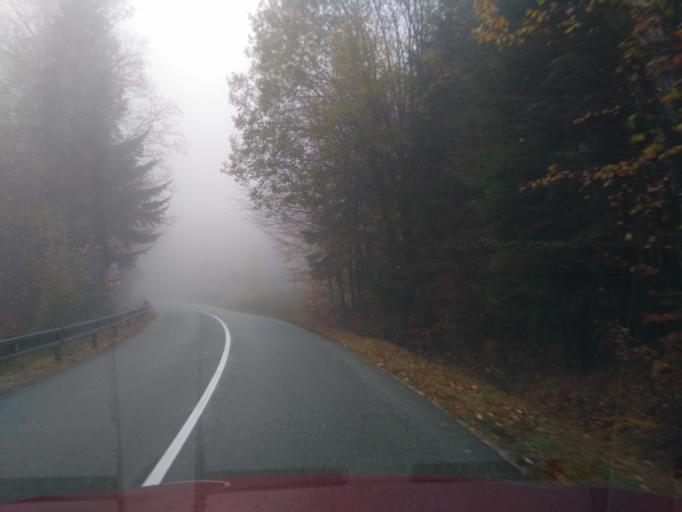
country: SK
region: Kosicky
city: Medzev
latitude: 48.7248
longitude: 20.7704
